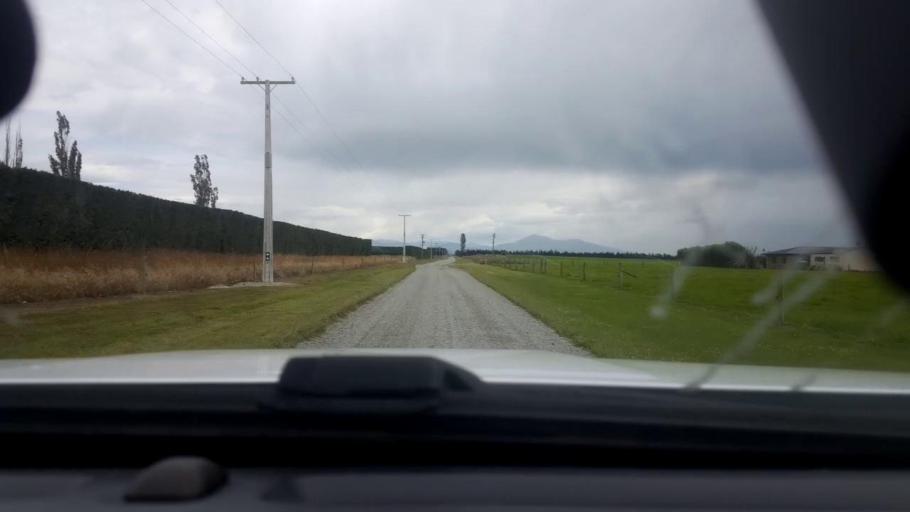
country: NZ
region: Canterbury
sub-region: Timaru District
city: Timaru
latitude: -44.1738
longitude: 171.4179
